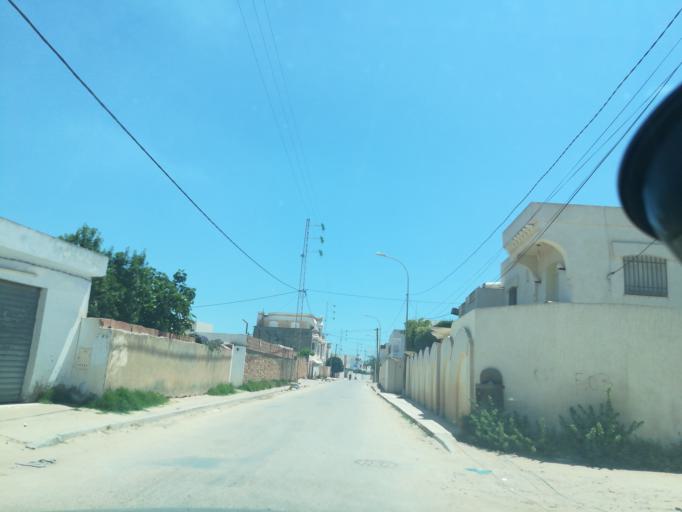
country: TN
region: Safaqis
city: Al Qarmadah
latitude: 34.8201
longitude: 10.7579
